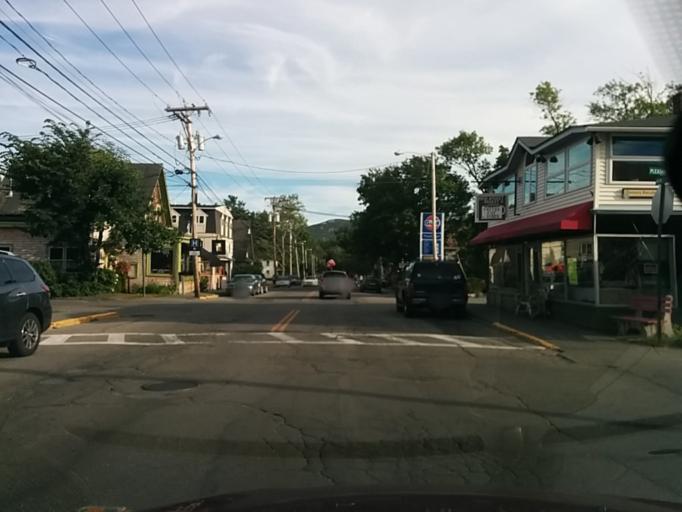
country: US
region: Maine
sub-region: Hancock County
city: Bar Harbor
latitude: 44.3845
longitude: -68.2035
